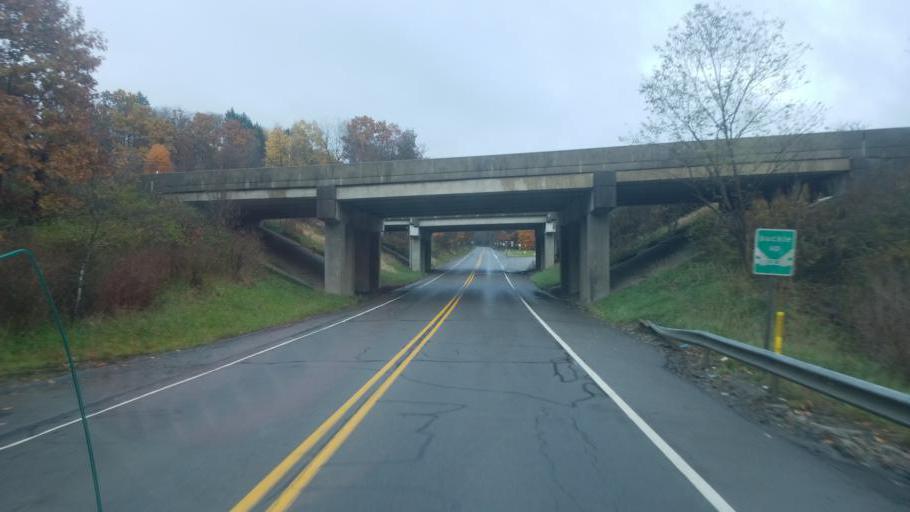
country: US
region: Pennsylvania
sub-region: Clarion County
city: Knox
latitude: 41.1841
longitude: -79.6755
